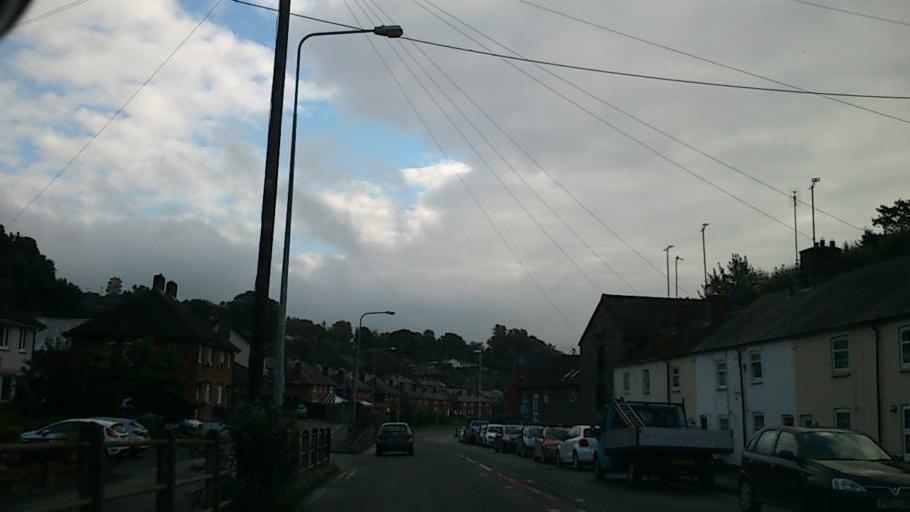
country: GB
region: Wales
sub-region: Sir Powys
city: Welshpool
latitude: 52.6618
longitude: -3.1547
